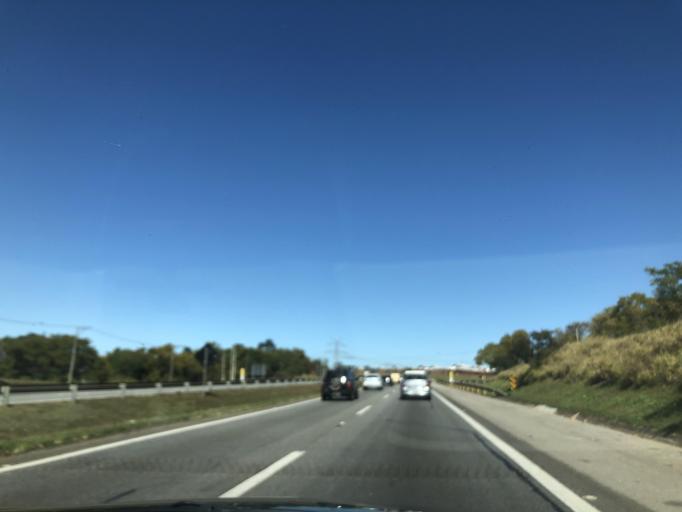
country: BR
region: Sao Paulo
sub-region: Sorocaba
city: Sorocaba
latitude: -23.4466
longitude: -47.3866
